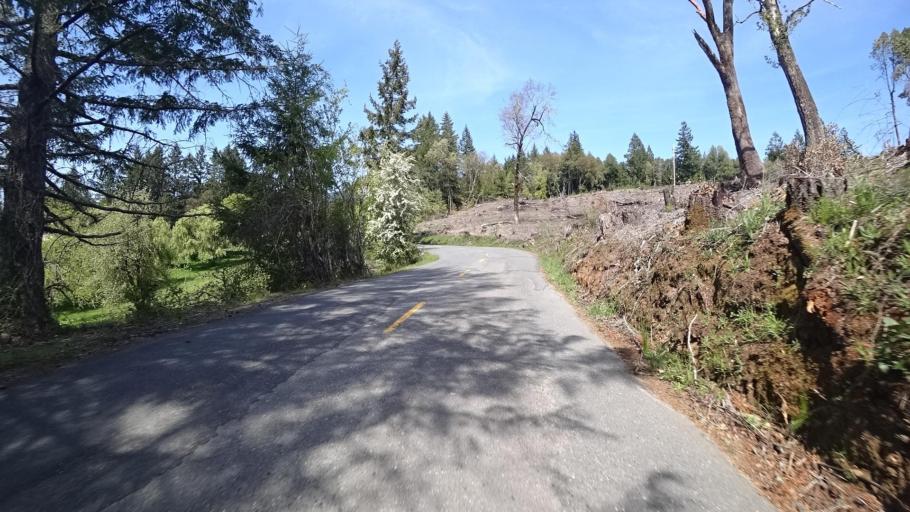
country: US
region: California
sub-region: Humboldt County
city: Redway
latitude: 40.3819
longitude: -123.7433
